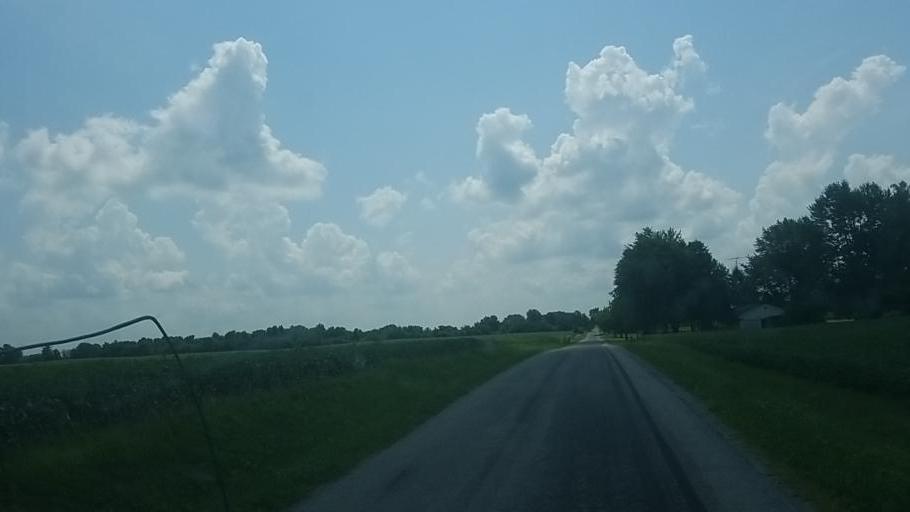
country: US
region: Ohio
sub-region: Marion County
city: Marion
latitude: 40.7306
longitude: -83.1499
